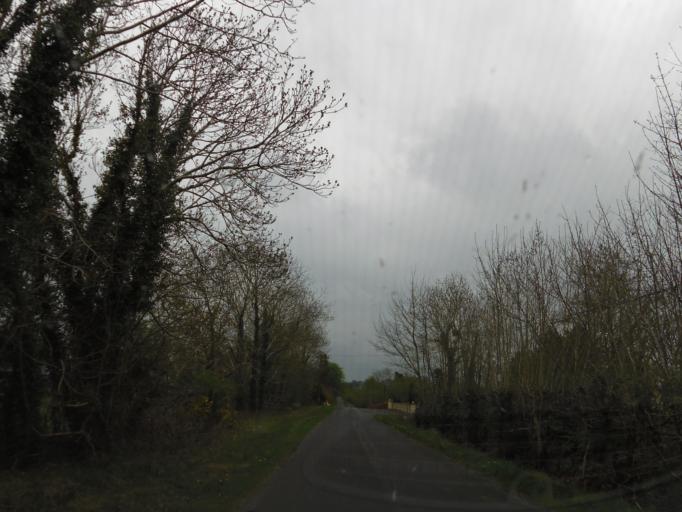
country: IE
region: Connaught
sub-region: Maigh Eo
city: Claremorris
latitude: 53.7822
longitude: -8.9608
